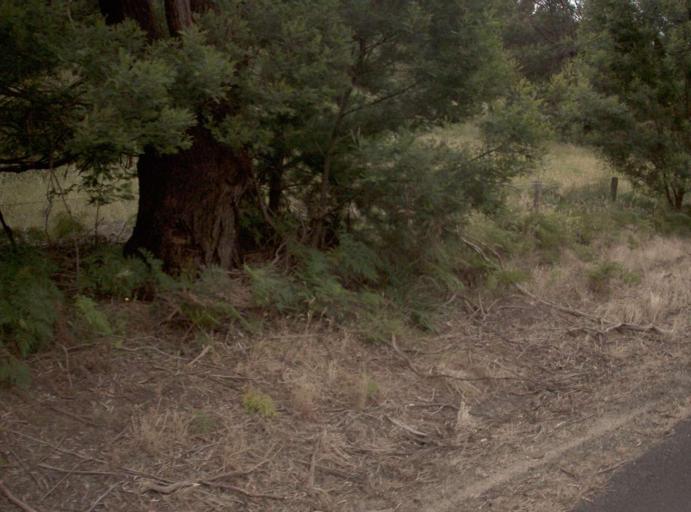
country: AU
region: Victoria
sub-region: Wellington
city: Sale
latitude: -38.2186
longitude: 147.0597
